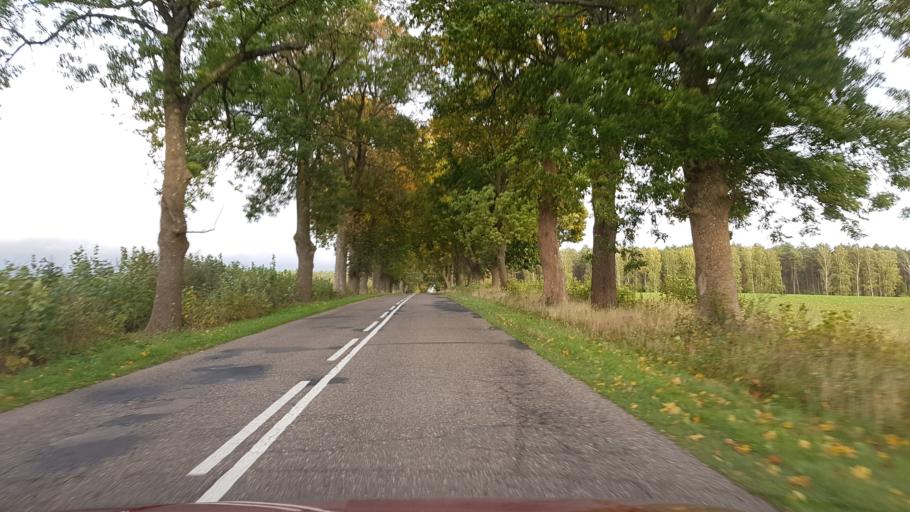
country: PL
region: West Pomeranian Voivodeship
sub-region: Powiat walecki
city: Tuczno
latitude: 53.1632
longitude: 16.2639
